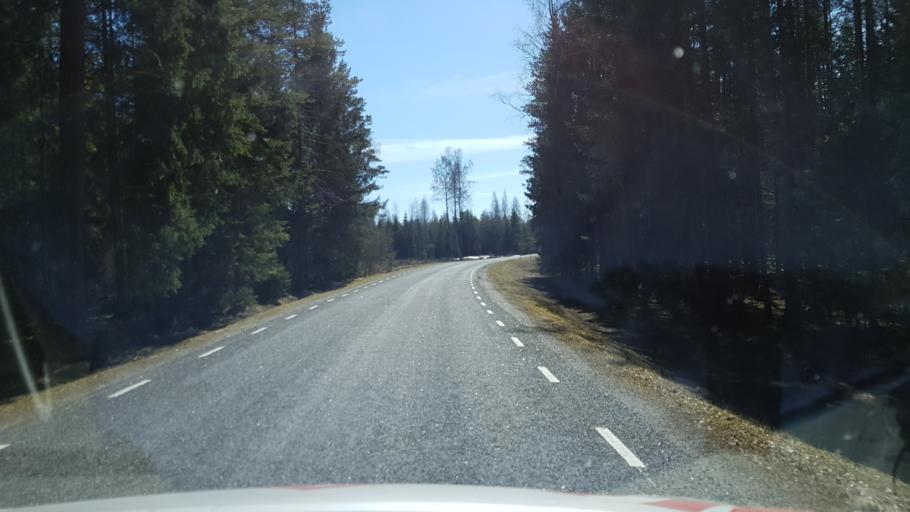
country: EE
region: Laeaene-Virumaa
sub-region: Vinni vald
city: Vinni
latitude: 59.1403
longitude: 26.5246
